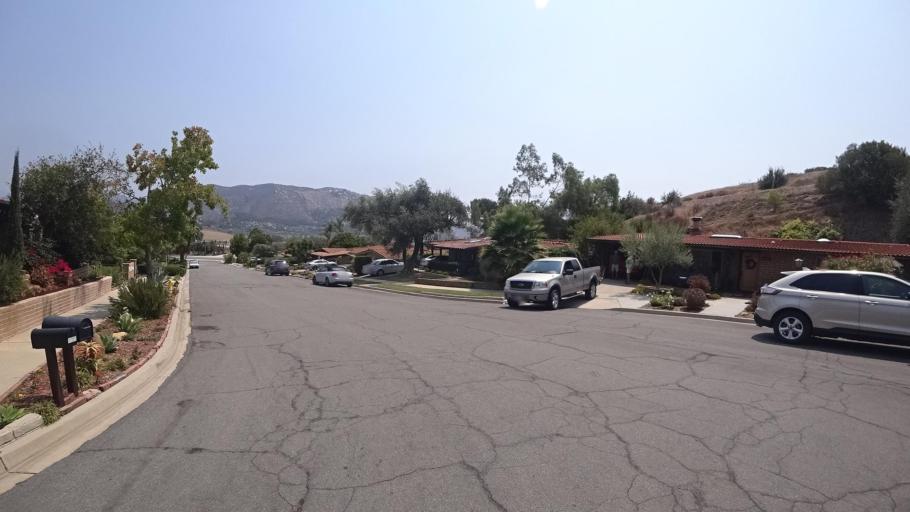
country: US
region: California
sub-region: San Diego County
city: Bonsall
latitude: 33.3310
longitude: -117.1639
